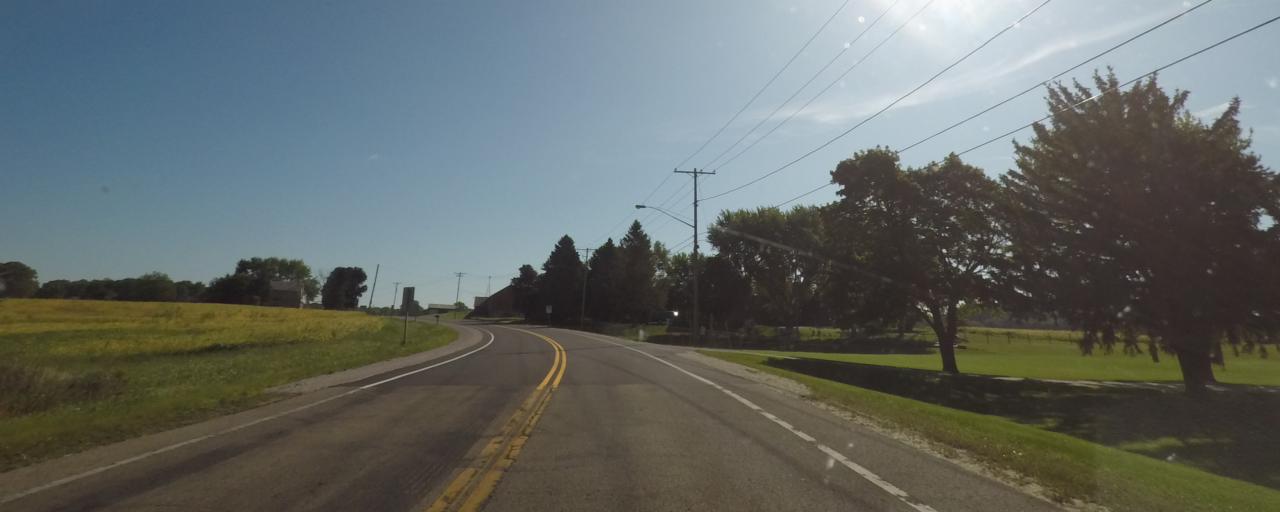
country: US
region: Wisconsin
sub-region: Jefferson County
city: Johnson Creek
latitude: 43.0119
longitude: -88.6968
